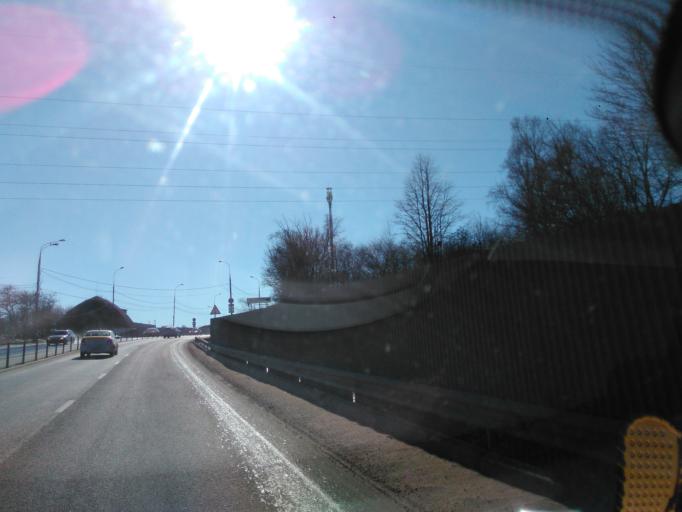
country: RU
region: Moskovskaya
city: Iksha
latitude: 56.1630
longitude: 37.5000
